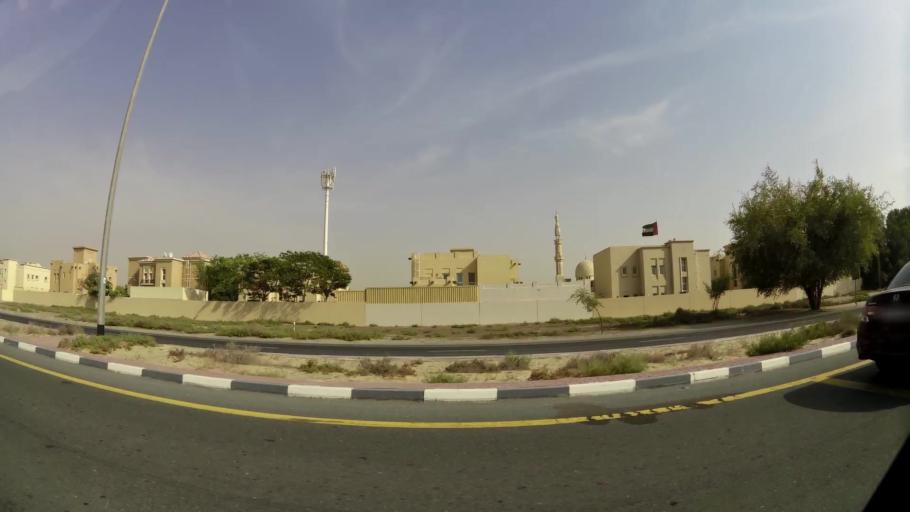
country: AE
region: Ash Shariqah
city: Sharjah
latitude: 25.2708
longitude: 55.4479
